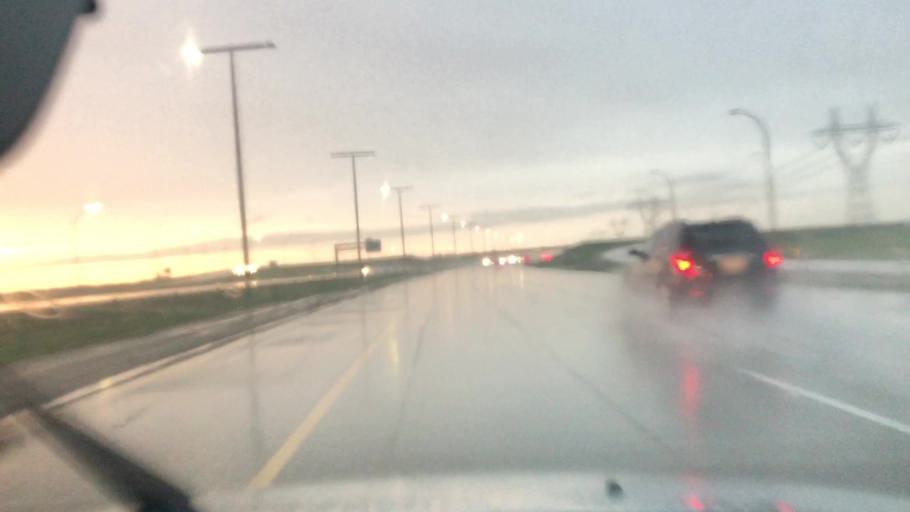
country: CA
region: Alberta
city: Devon
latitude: 53.4379
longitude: -113.5953
